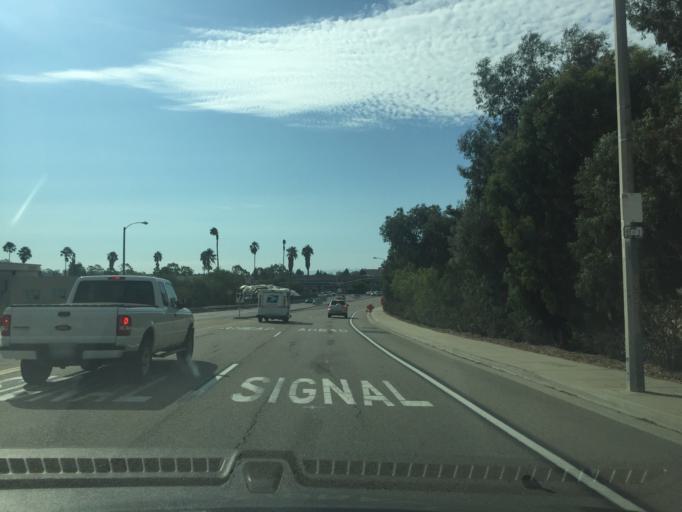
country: US
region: California
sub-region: Santa Barbara County
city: Isla Vista
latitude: 34.4326
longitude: -119.8700
